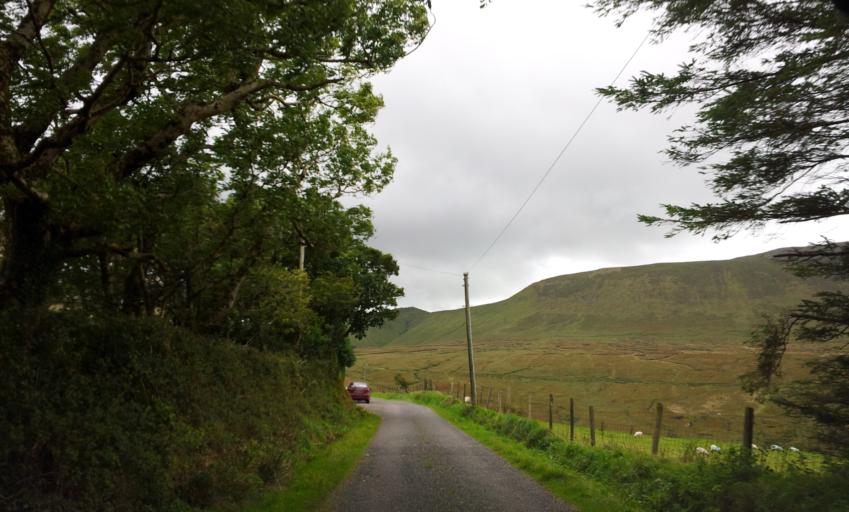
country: IE
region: Munster
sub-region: Ciarrai
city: Killorglin
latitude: 52.1956
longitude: -9.9299
